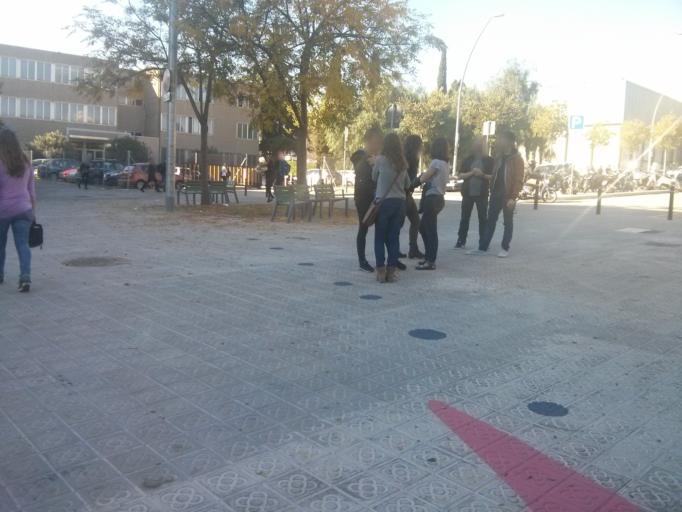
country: ES
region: Catalonia
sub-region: Provincia de Barcelona
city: les Corts
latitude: 41.3823
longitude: 2.1176
